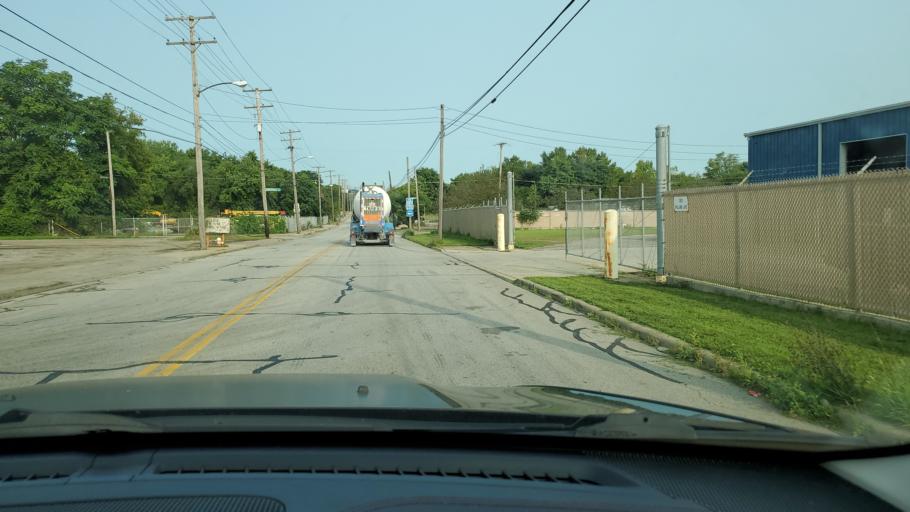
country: US
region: Ohio
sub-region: Mahoning County
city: Youngstown
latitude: 41.0821
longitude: -80.6318
